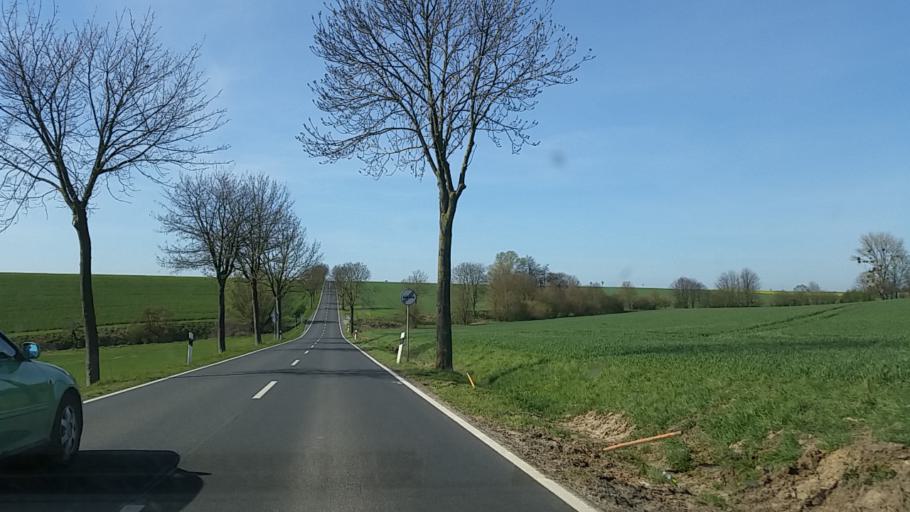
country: DE
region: Lower Saxony
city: Twieflingen
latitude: 52.1170
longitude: 10.9363
